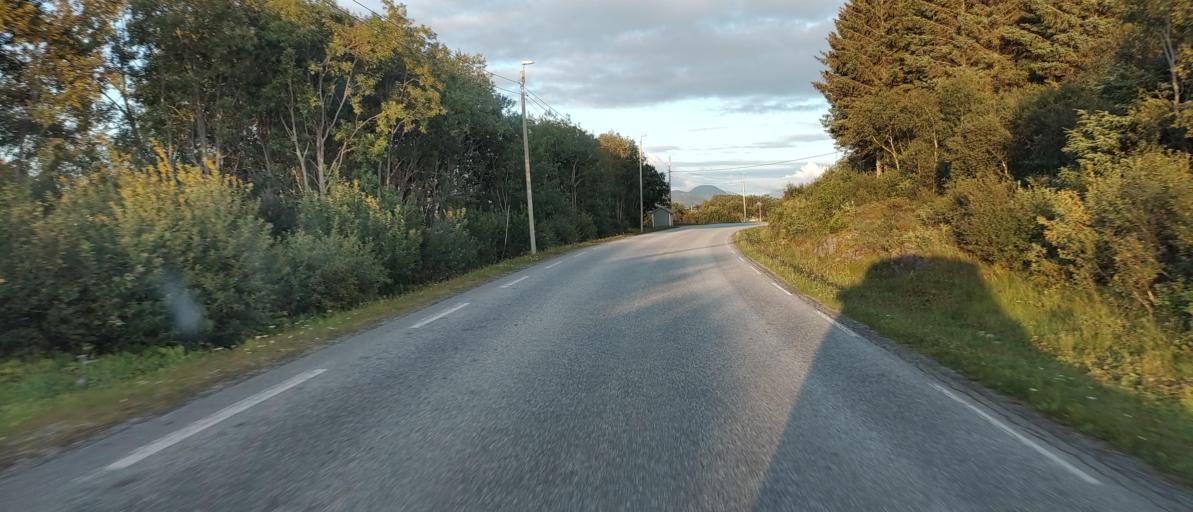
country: NO
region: More og Romsdal
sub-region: Fraena
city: Elnesvagen
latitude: 62.9914
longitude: 7.1934
